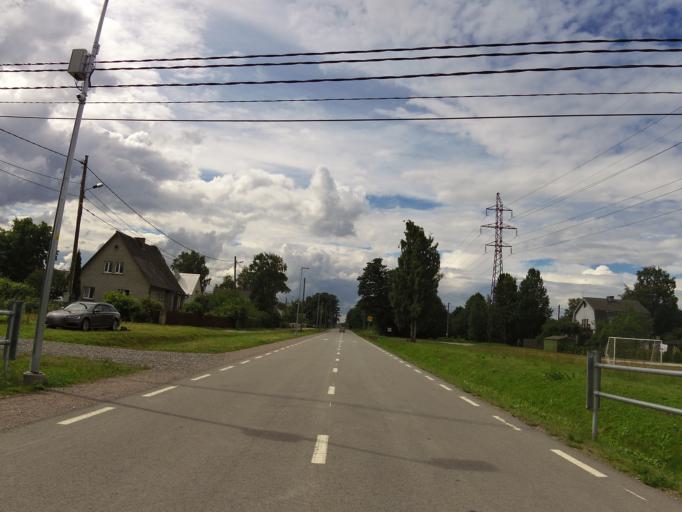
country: EE
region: Harju
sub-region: Tallinna linn
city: Tallinn
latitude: 59.4269
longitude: 24.6826
